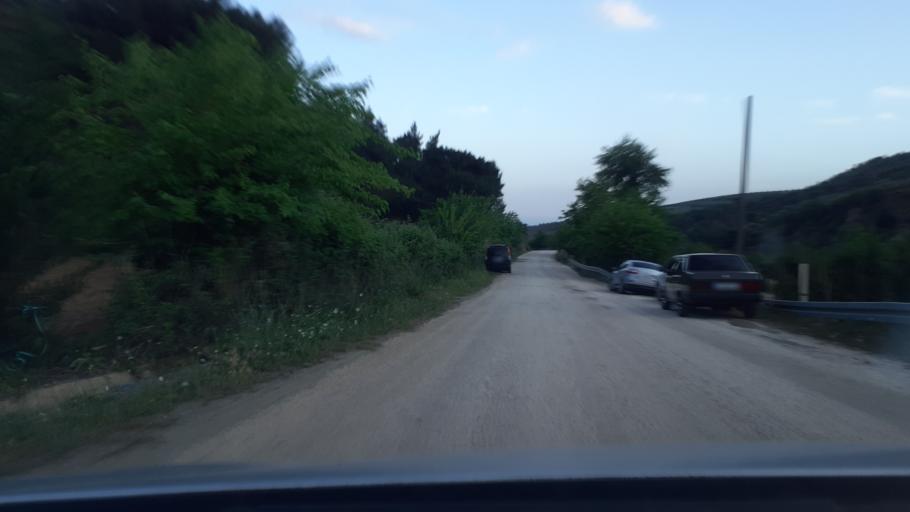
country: TR
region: Hatay
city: Kirikhan
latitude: 36.5207
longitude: 36.3182
